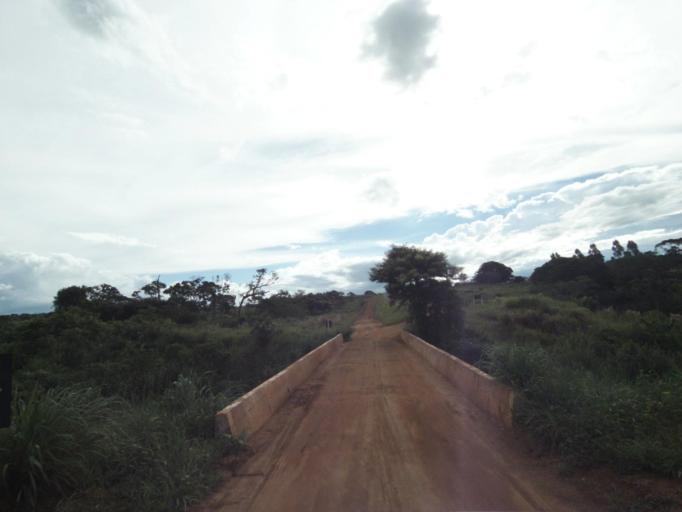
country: BR
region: Goias
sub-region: Jaragua
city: Jaragua
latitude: -15.8806
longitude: -49.4298
